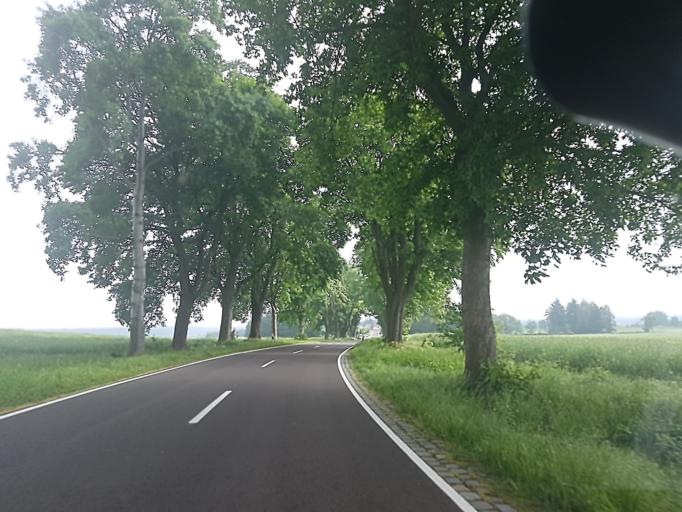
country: DE
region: Brandenburg
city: Gorzke
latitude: 52.0640
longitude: 12.2956
